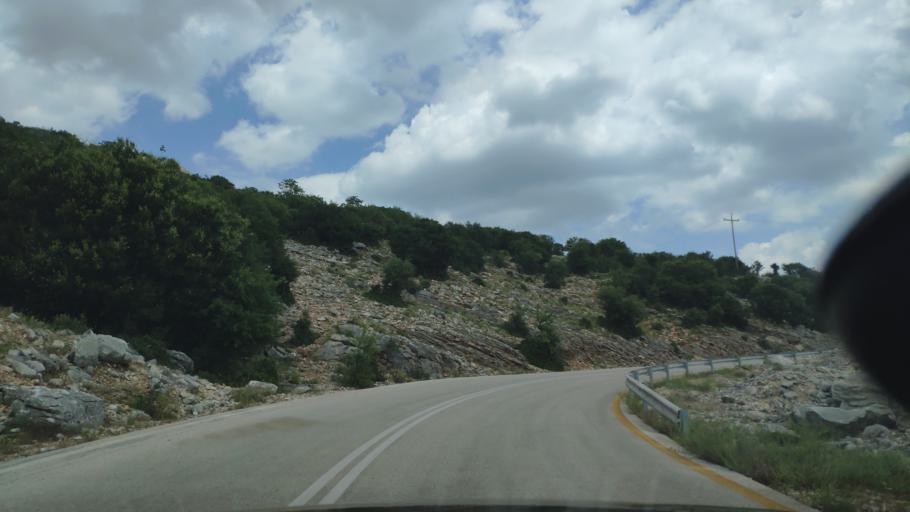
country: GR
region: Epirus
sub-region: Nomos Artas
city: Grammenitsa
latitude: 39.2767
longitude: 20.9747
